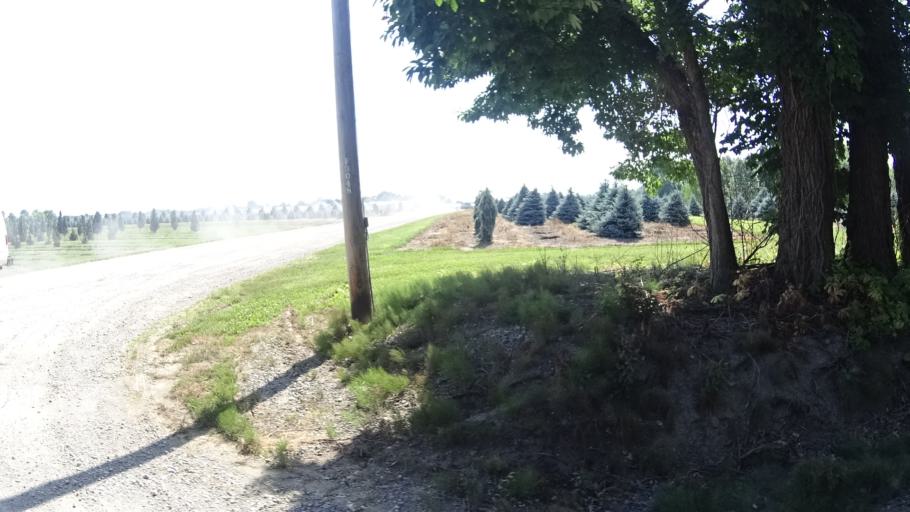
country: US
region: Ohio
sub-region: Erie County
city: Huron
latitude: 41.3748
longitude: -82.4720
